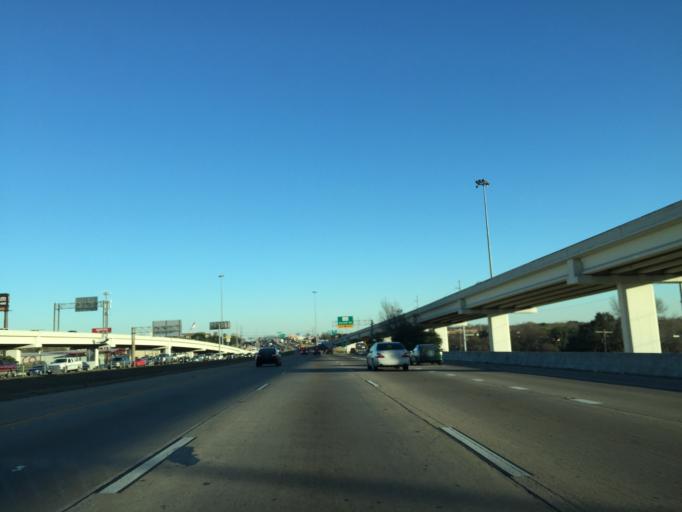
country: US
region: Texas
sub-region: Williamson County
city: Jollyville
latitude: 30.3778
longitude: -97.7357
